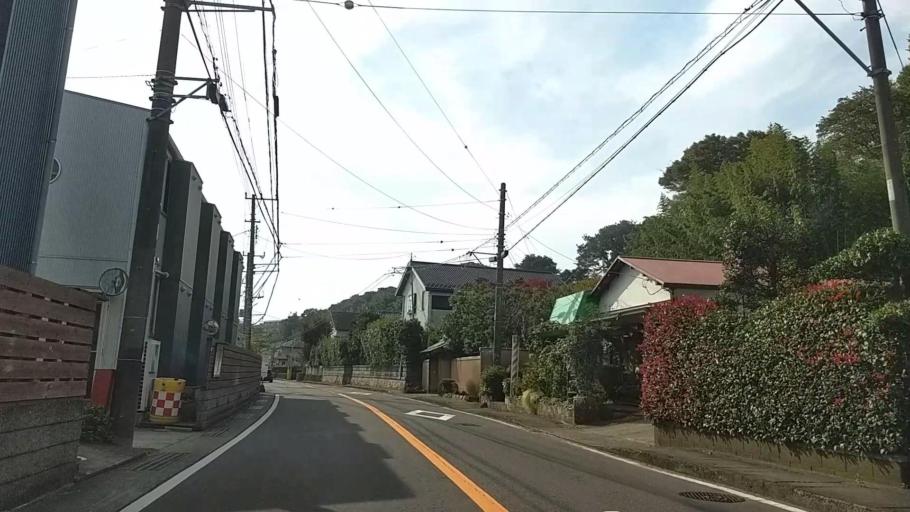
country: JP
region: Kanagawa
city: Atsugi
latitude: 35.4506
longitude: 139.3519
